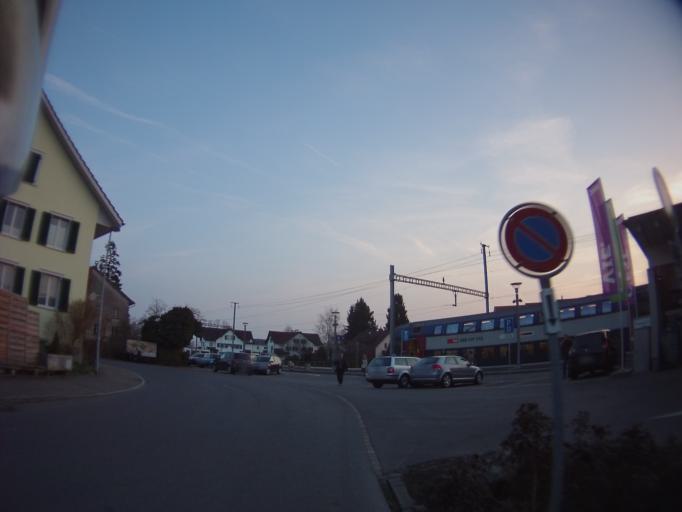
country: CH
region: Zurich
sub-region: Bezirk Affoltern
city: Mettmenstetten
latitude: 47.2438
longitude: 8.4577
